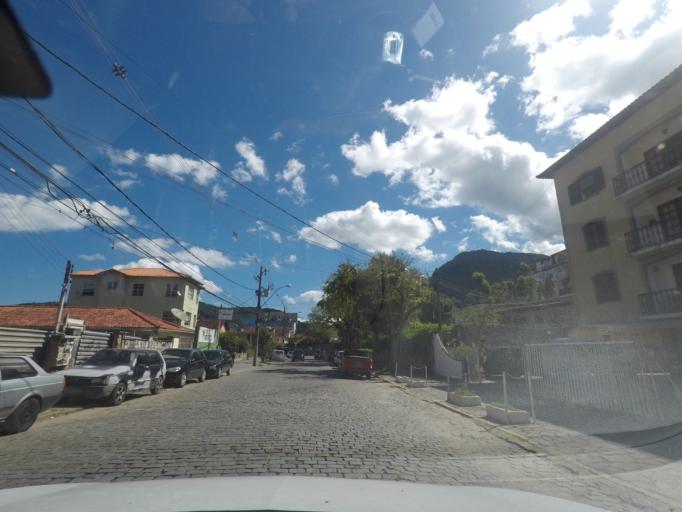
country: BR
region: Rio de Janeiro
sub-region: Teresopolis
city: Teresopolis
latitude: -22.4443
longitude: -42.9789
